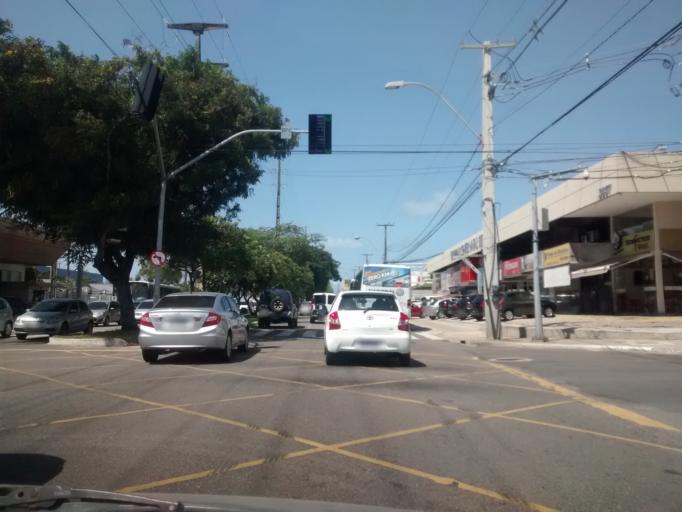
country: BR
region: Rio Grande do Norte
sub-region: Natal
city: Natal
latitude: -5.8165
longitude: -35.2117
